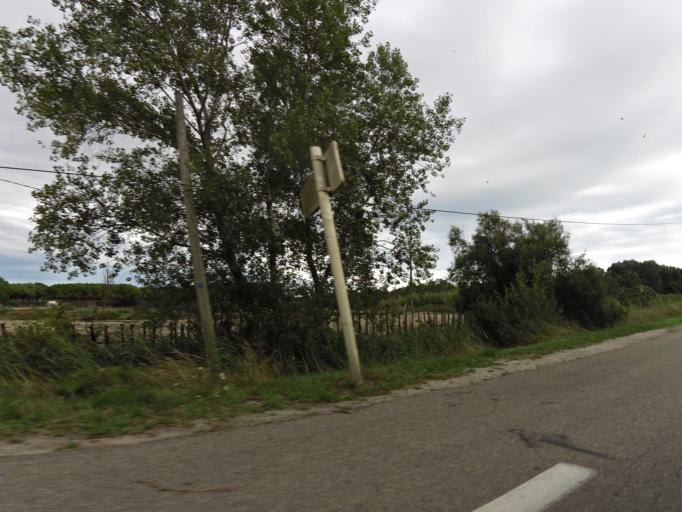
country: FR
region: Languedoc-Roussillon
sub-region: Departement du Gard
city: Le Grau-du-Roi
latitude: 43.5607
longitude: 4.1562
